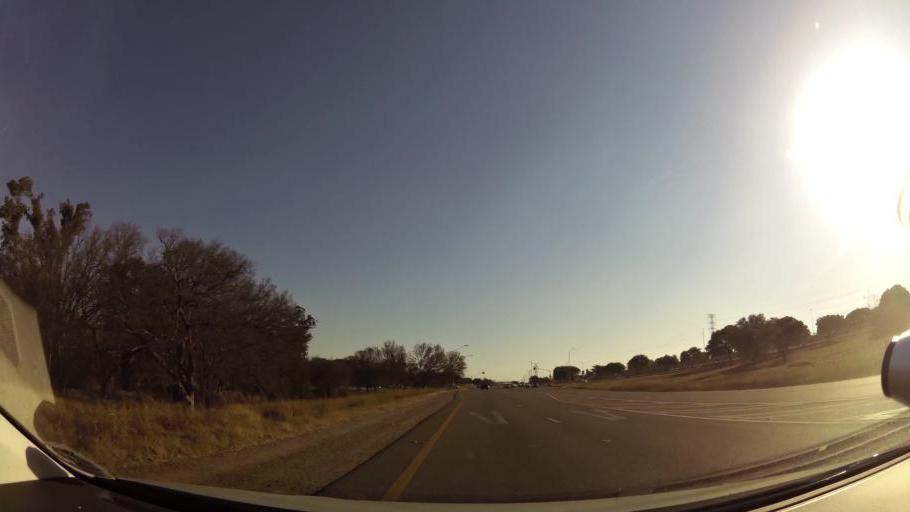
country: ZA
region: Gauteng
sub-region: City of Tshwane Metropolitan Municipality
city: Pretoria
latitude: -25.7460
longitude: 28.1346
